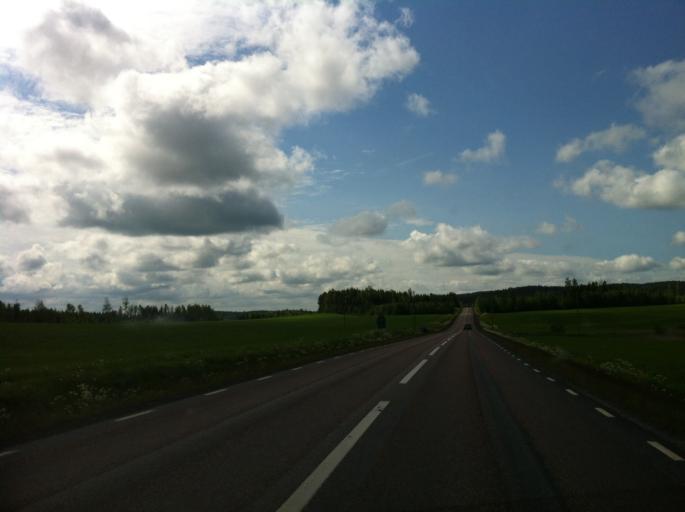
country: SE
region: Vaermland
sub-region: Karlstads Kommun
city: Edsvalla
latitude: 59.6324
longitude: 13.1595
